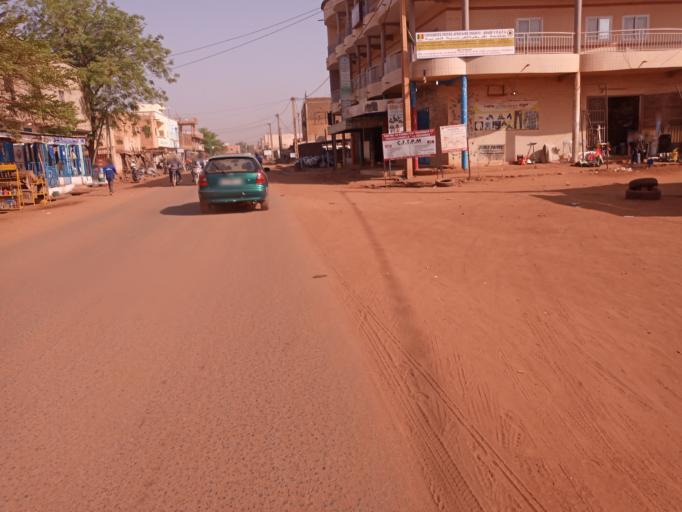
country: ML
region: Bamako
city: Bamako
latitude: 12.5830
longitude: -7.9582
